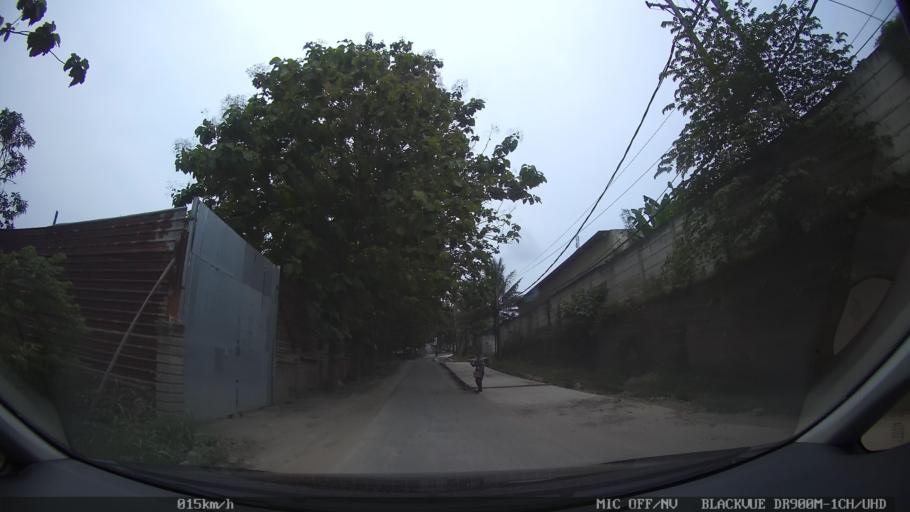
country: ID
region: Lampung
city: Bandarlampung
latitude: -5.4068
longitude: 105.3155
